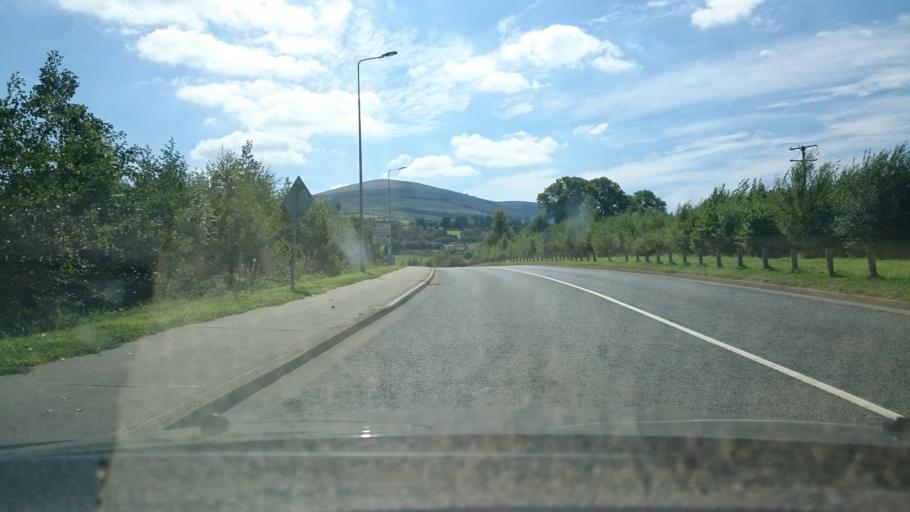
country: IE
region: Leinster
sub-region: Kilkenny
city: Graiguenamanagh
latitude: 52.5409
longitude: -6.9635
